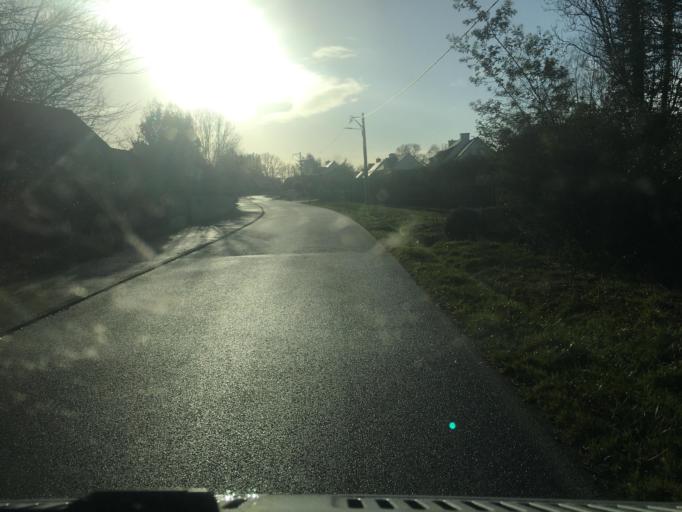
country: FR
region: Brittany
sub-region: Departement du Morbihan
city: Surzur
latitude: 47.5096
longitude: -2.6791
